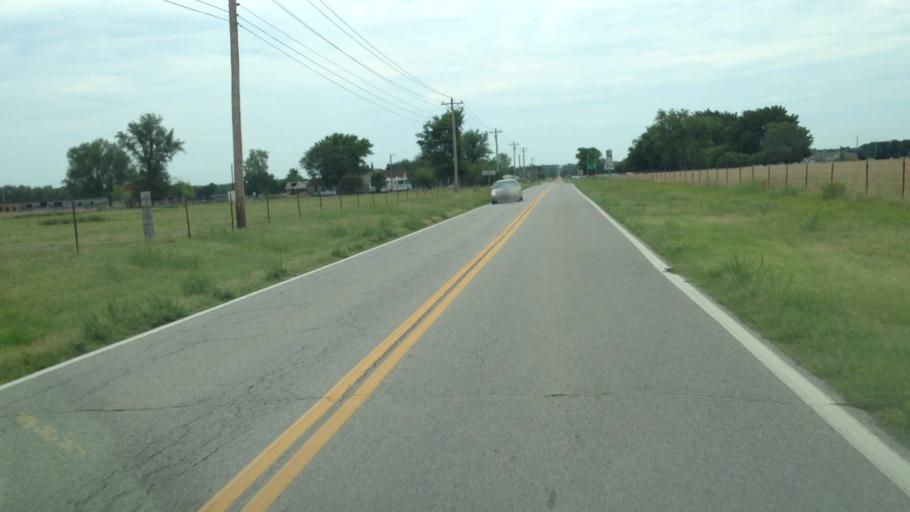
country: US
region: Oklahoma
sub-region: Delaware County
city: Cleora
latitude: 36.6094
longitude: -94.9634
